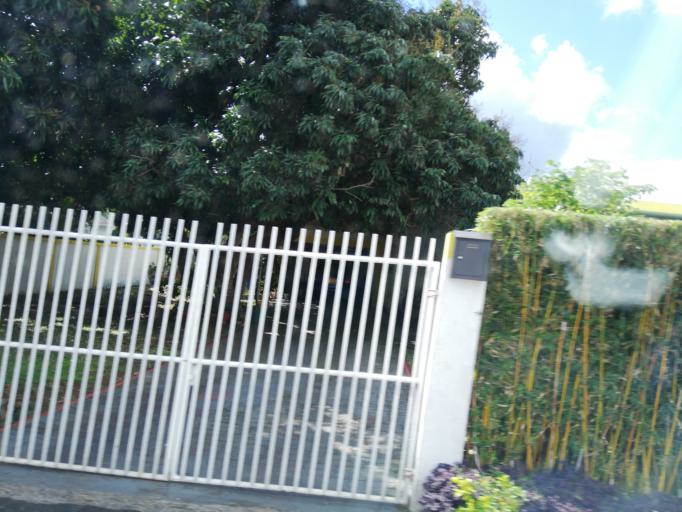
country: MU
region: Moka
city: Moka
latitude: -20.2206
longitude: 57.4747
